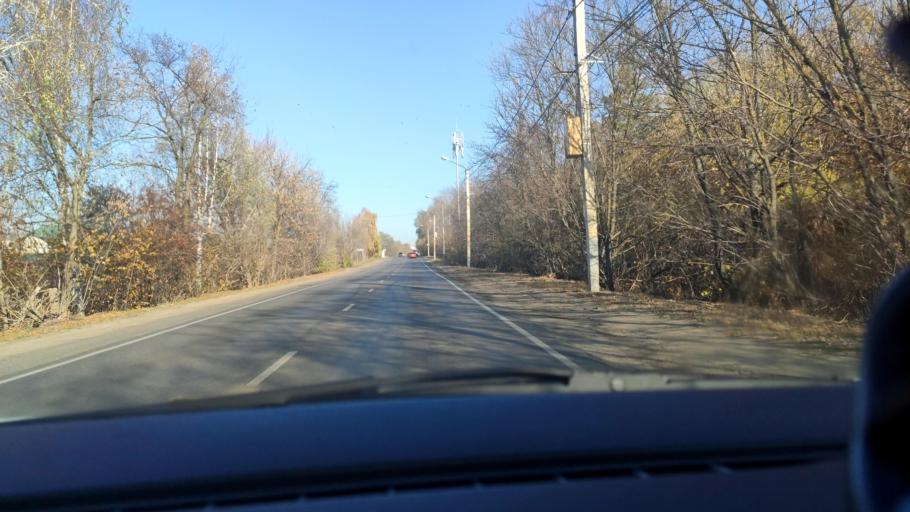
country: RU
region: Voronezj
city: Pridonskoy
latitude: 51.6362
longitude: 39.0859
